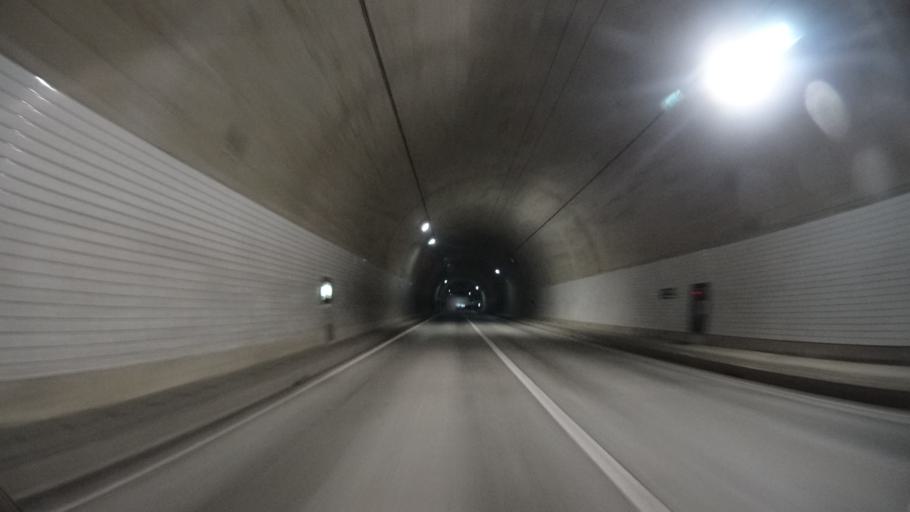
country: JP
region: Ehime
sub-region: Nishiuwa-gun
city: Ikata-cho
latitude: 33.4549
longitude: 132.2740
